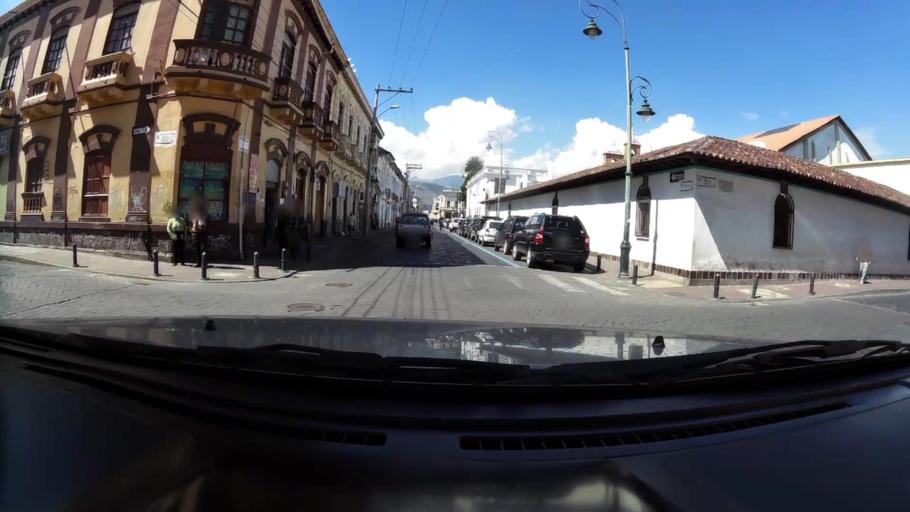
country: EC
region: Chimborazo
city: Riobamba
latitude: -1.6721
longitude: -78.6473
